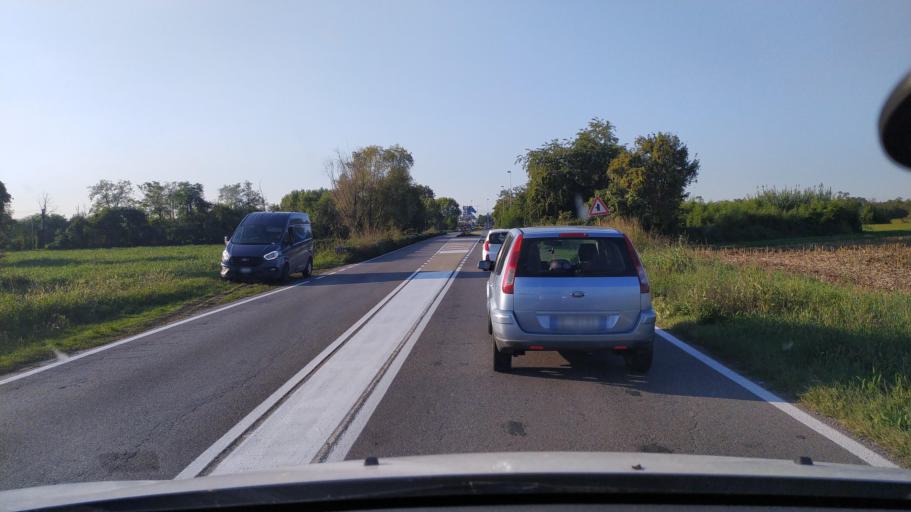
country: IT
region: Lombardy
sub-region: Citta metropolitana di Milano
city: Vittuone
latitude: 45.4766
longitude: 8.9543
